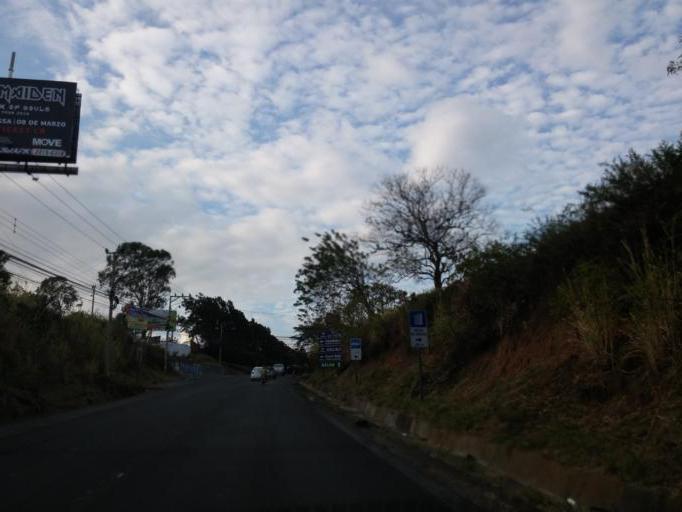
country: CR
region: Heredia
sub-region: Canton de Belen
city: San Antonio
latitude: 9.9672
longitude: -84.1996
